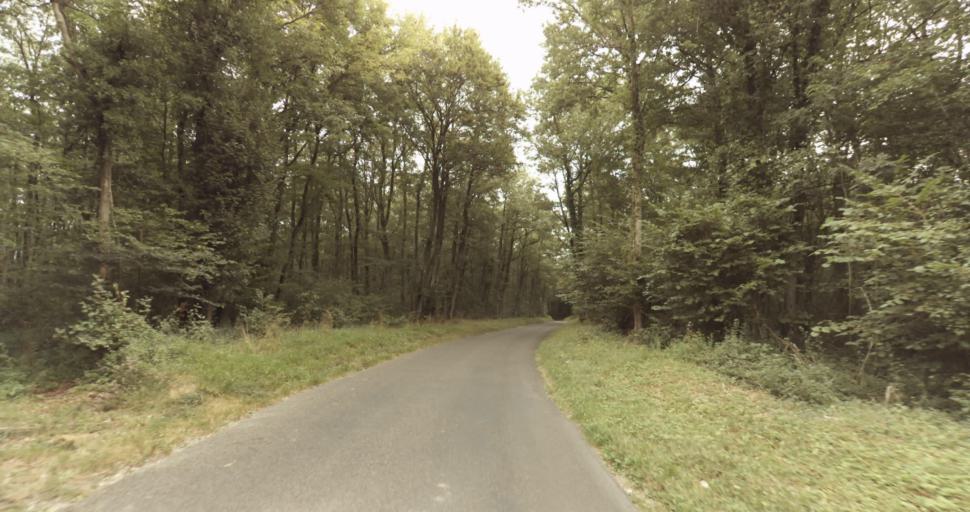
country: FR
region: Haute-Normandie
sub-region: Departement de l'Eure
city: Menilles
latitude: 49.0316
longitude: 1.3109
